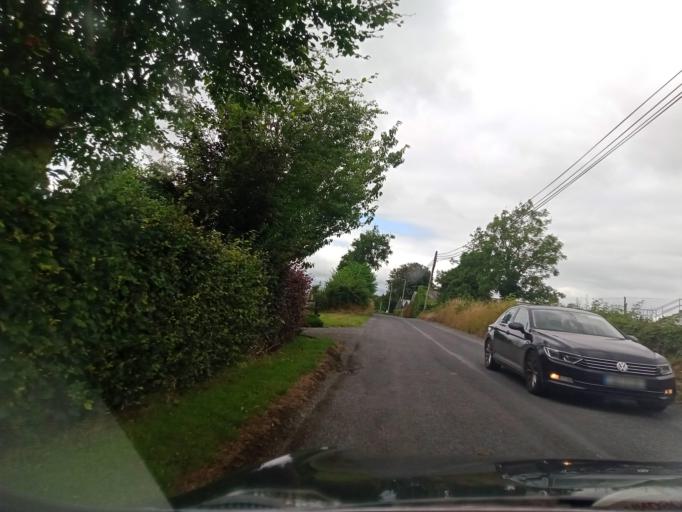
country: IE
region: Leinster
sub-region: Laois
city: Stradbally
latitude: 52.9745
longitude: -7.1792
